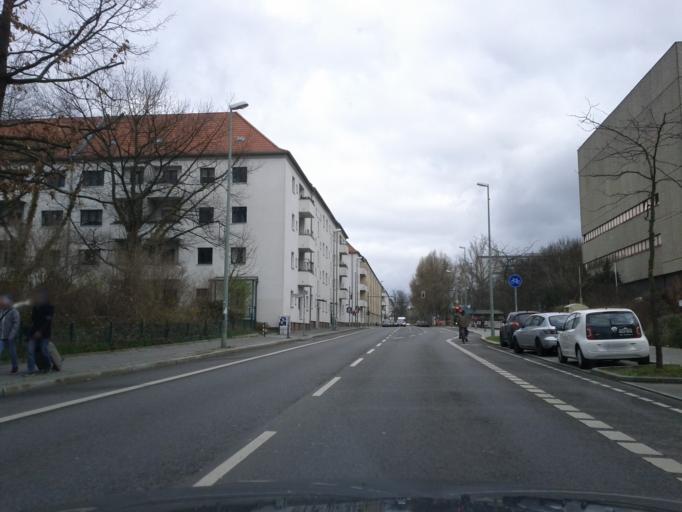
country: DE
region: Berlin
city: Lichtenberg
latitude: 52.5149
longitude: 13.4849
